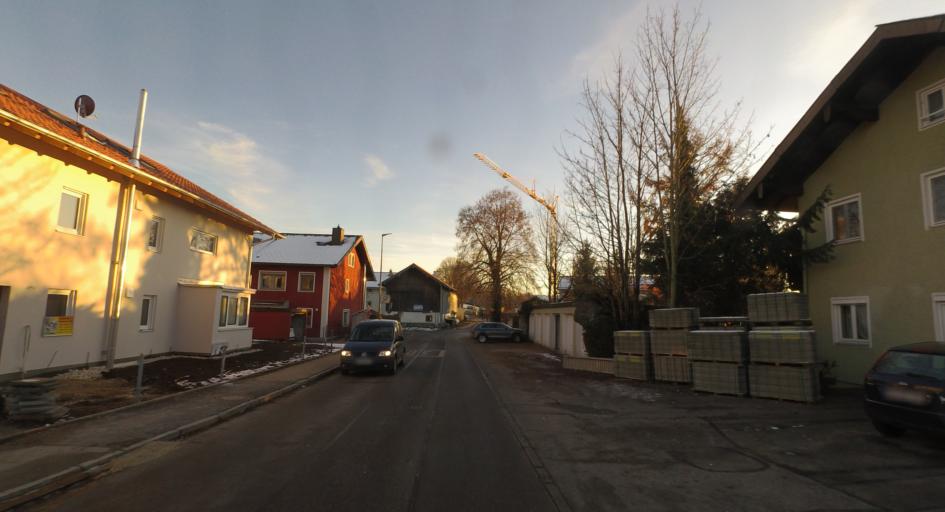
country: DE
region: Bavaria
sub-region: Upper Bavaria
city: Traunstein
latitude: 47.8774
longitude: 12.6282
